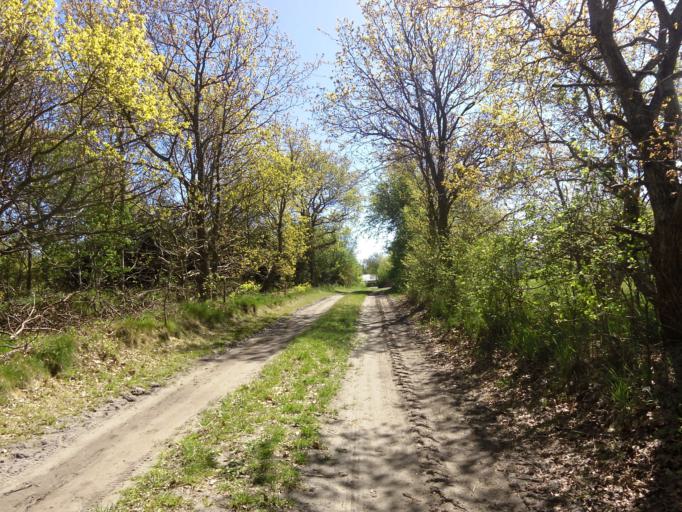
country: DK
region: South Denmark
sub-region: Tonder Kommune
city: Sherrebek
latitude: 55.2319
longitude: 8.7327
